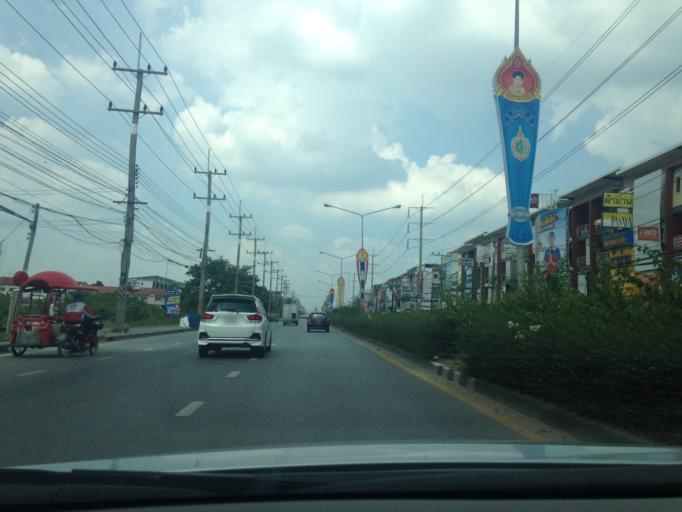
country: TH
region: Pathum Thani
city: Sam Khok
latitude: 14.0486
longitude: 100.5248
